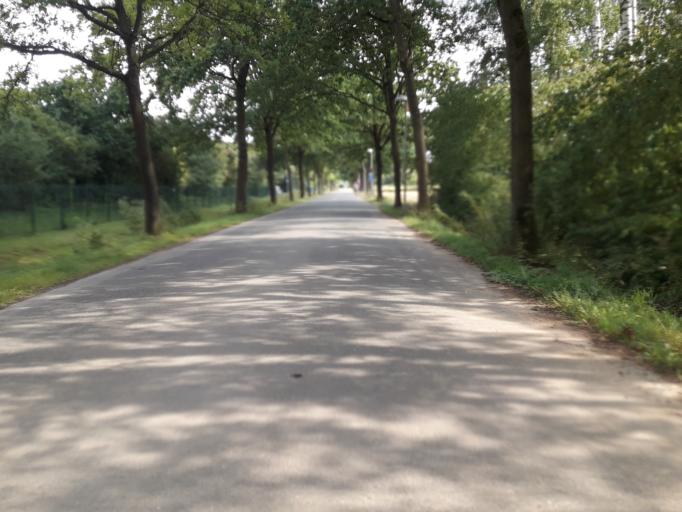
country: DE
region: North Rhine-Westphalia
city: Bad Lippspringe
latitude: 51.7658
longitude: 8.7997
